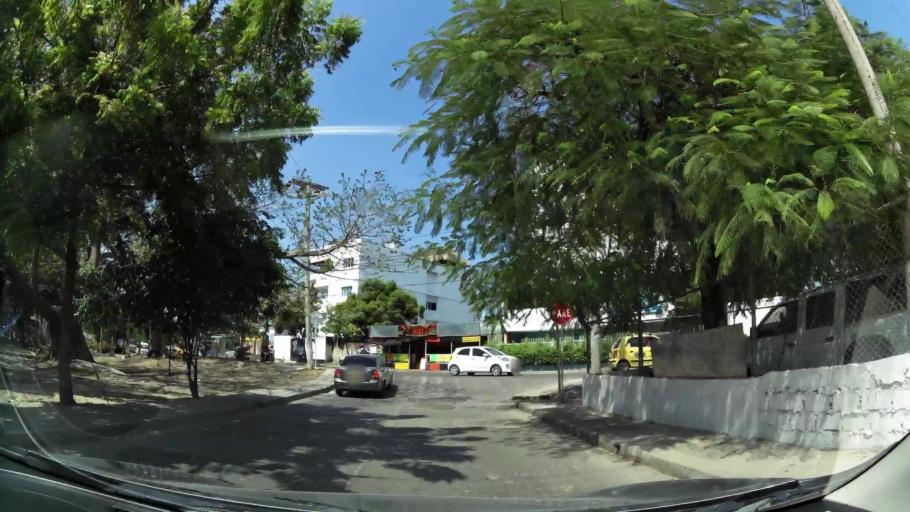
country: CO
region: Bolivar
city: Cartagena
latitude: 10.3945
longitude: -75.4917
